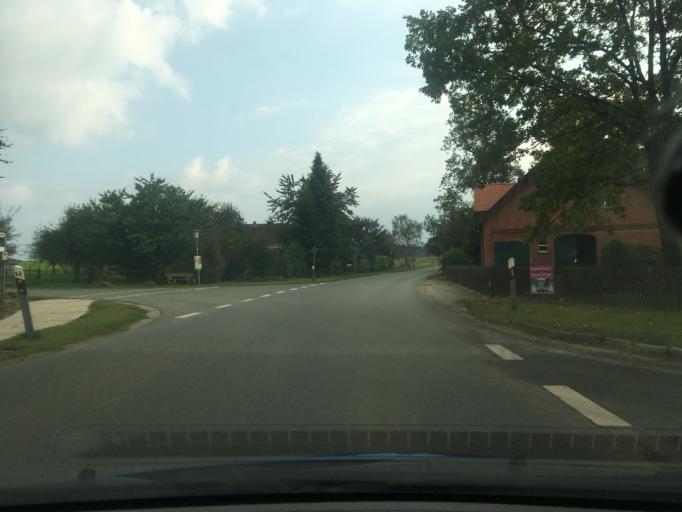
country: DE
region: Lower Saxony
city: Soderstorf
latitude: 53.1622
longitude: 10.1592
